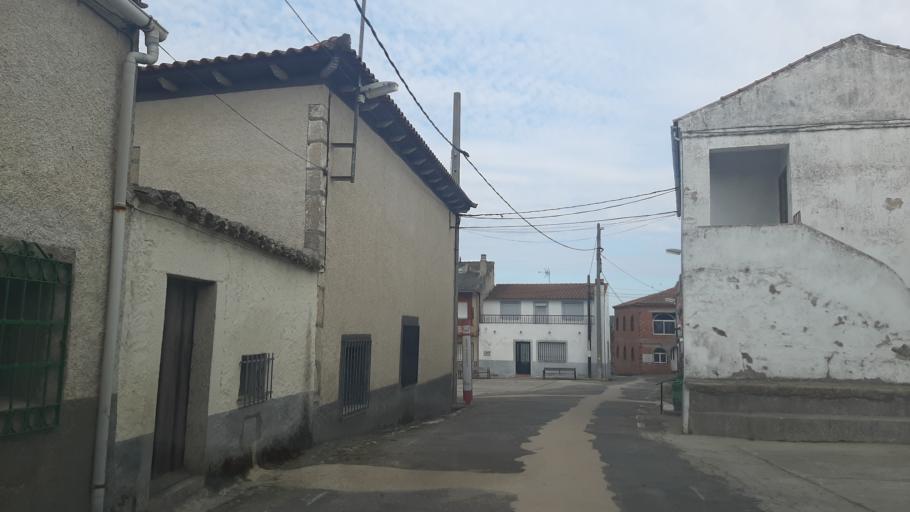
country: ES
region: Castille and Leon
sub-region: Provincia de Salamanca
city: Gallegos de Arganan
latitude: 40.6509
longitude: -6.7586
